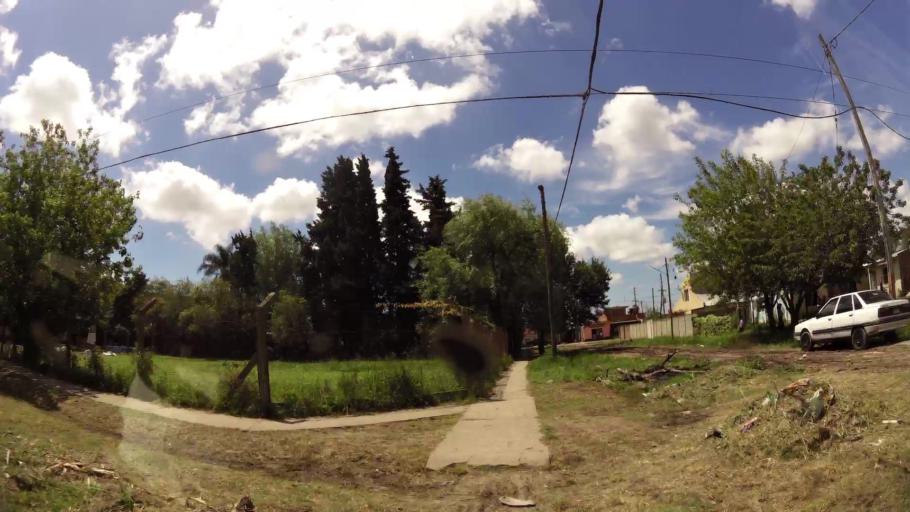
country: AR
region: Buenos Aires
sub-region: Partido de Quilmes
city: Quilmes
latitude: -34.8139
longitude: -58.2358
